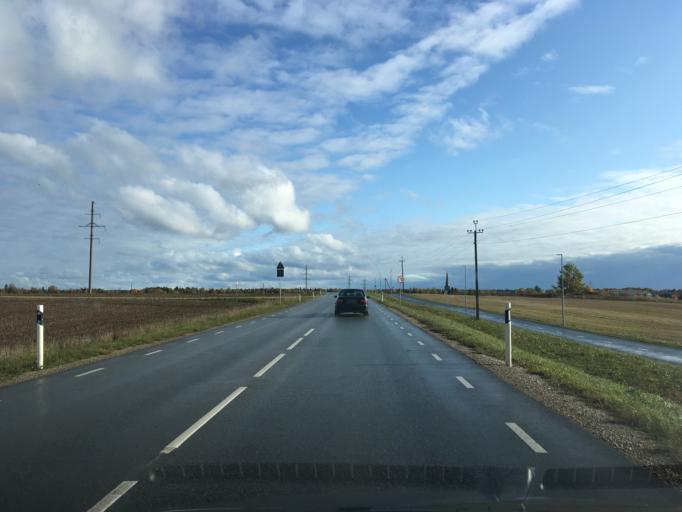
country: EE
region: Harju
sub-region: Raasiku vald
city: Raasiku
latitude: 59.1855
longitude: 25.1470
